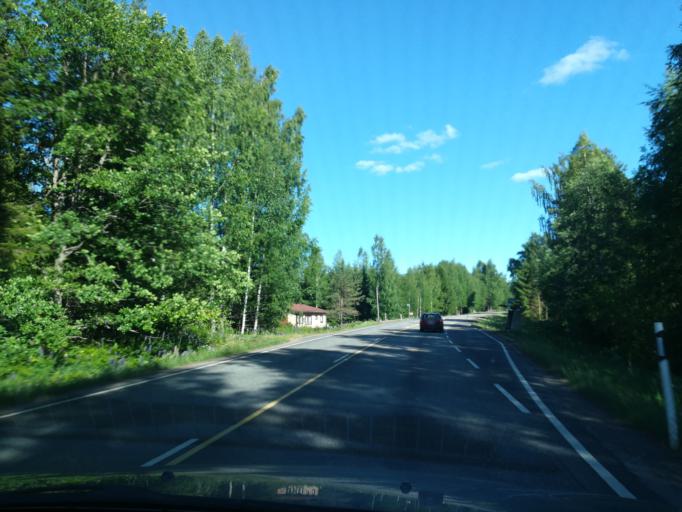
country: FI
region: South Karelia
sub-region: Imatra
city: Ruokolahti
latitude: 61.3713
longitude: 28.6716
